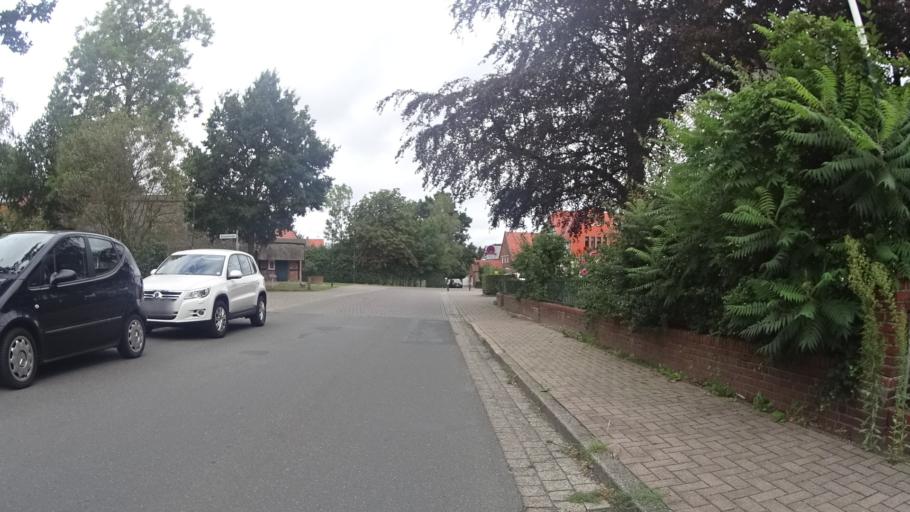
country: DE
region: Lower Saxony
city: Schiffdorf
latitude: 53.5335
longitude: 8.6547
